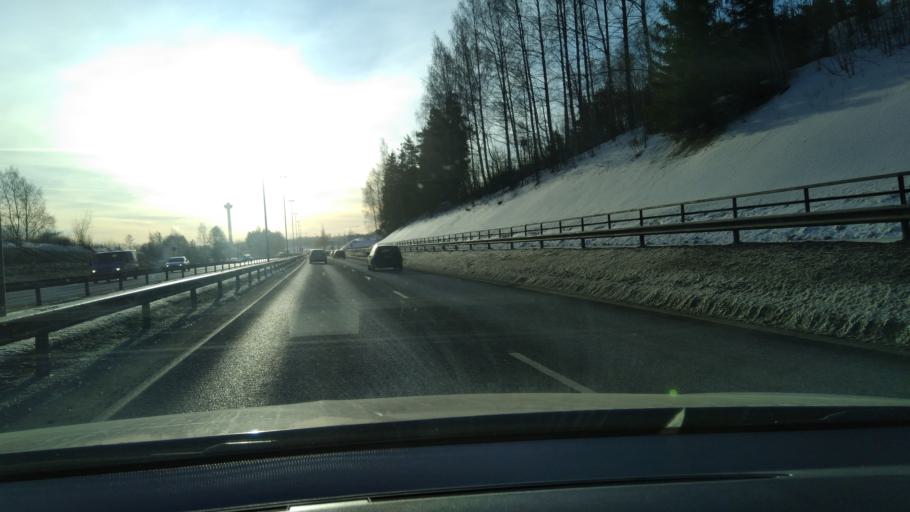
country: FI
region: Pirkanmaa
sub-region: Tampere
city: Tampere
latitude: 61.5077
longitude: 23.7030
